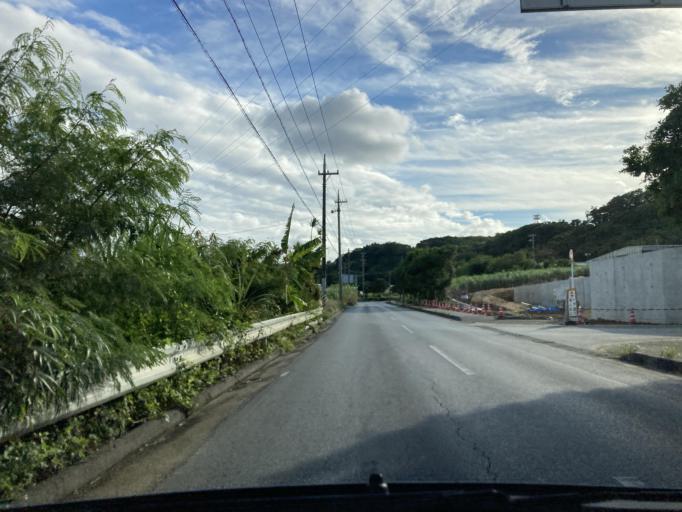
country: JP
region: Okinawa
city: Itoman
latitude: 26.1379
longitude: 127.7466
